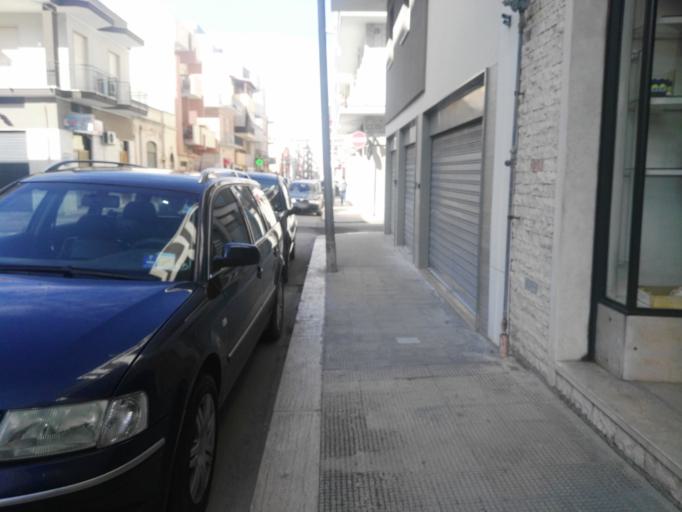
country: IT
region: Apulia
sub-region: Provincia di Barletta - Andria - Trani
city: Andria
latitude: 41.2199
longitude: 16.3050
